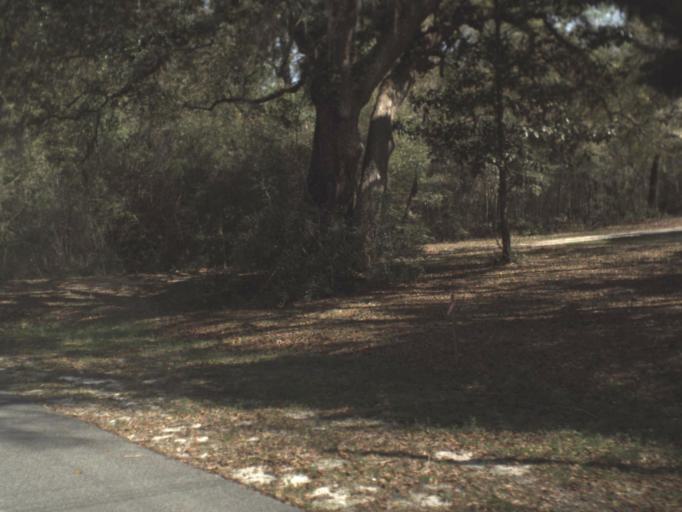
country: US
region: Florida
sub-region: Wakulla County
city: Crawfordville
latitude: 30.0684
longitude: -84.4569
